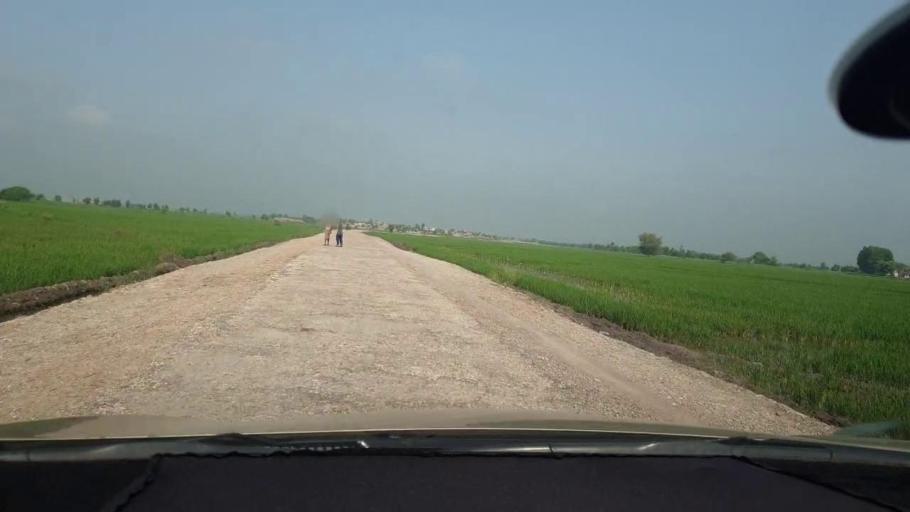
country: PK
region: Sindh
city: Kambar
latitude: 27.5385
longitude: 68.0549
